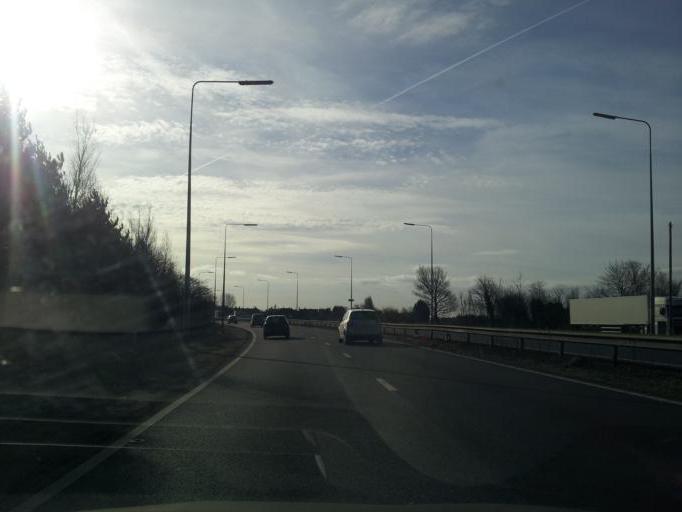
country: GB
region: England
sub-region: Central Bedfordshire
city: Sandy
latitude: 52.1095
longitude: -0.2826
